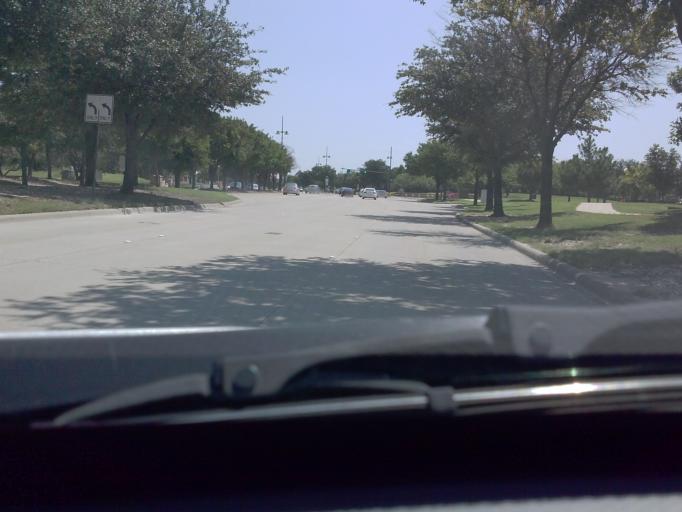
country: US
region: Texas
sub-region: Collin County
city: Frisco
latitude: 33.1012
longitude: -96.8176
